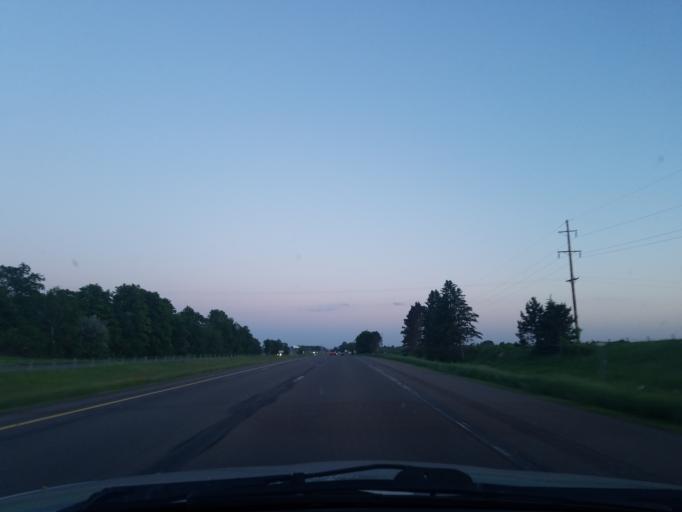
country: US
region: Minnesota
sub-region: Pine County
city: Rock Creek
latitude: 45.7819
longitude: -92.9906
